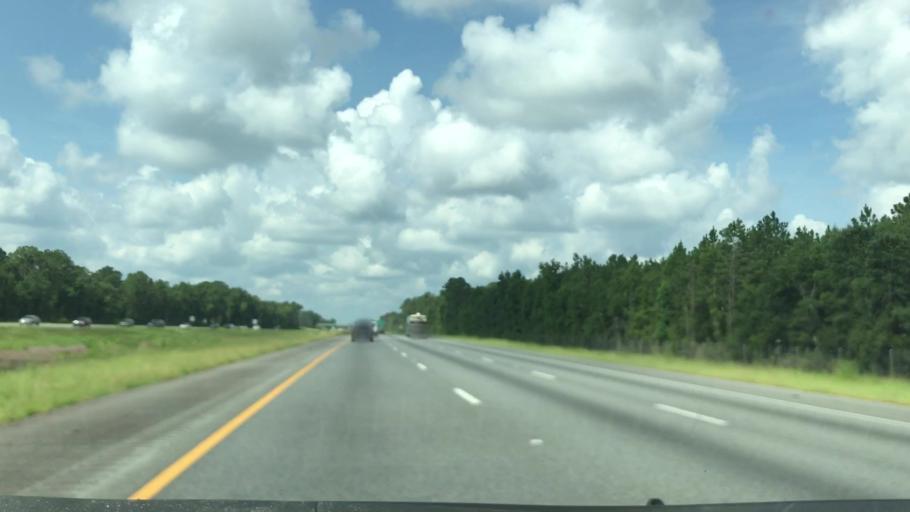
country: US
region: Georgia
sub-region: Camden County
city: Woodbine
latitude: 31.0660
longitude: -81.6305
